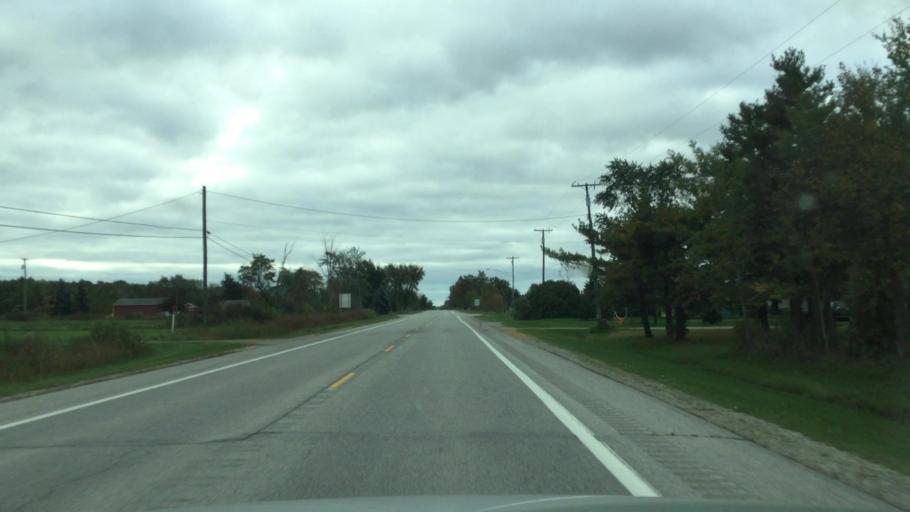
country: US
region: Michigan
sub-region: Macomb County
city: Memphis
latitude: 42.9571
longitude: -82.7633
